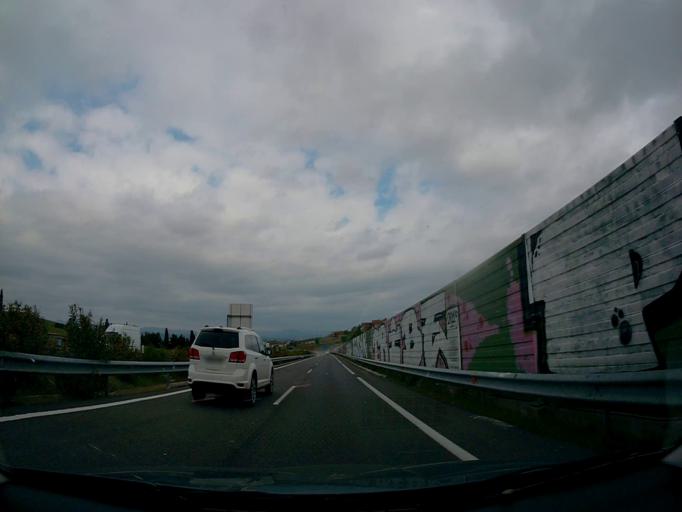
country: ES
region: Madrid
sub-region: Provincia de Madrid
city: Brunete
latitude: 40.3978
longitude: -3.9995
